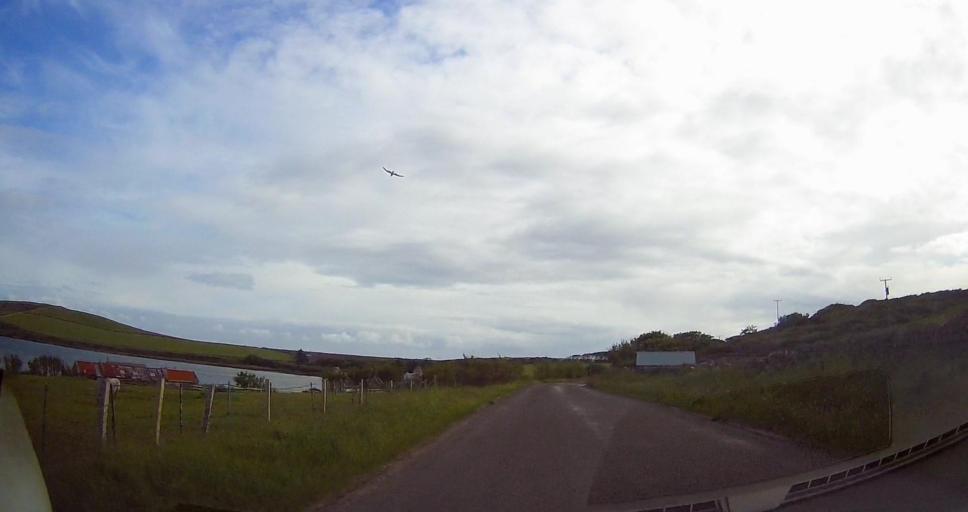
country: GB
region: Scotland
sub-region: Orkney Islands
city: Stromness
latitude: 58.7902
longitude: -3.2588
